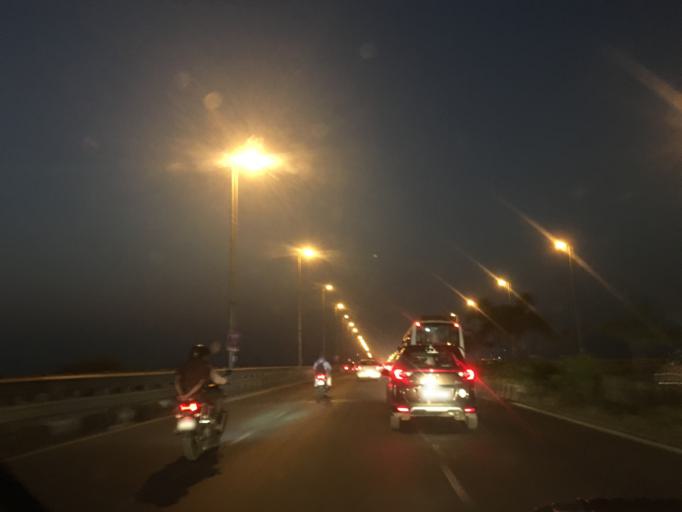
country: IN
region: Maharashtra
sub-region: Thane
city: Airoli
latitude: 19.1500
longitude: 72.9845
